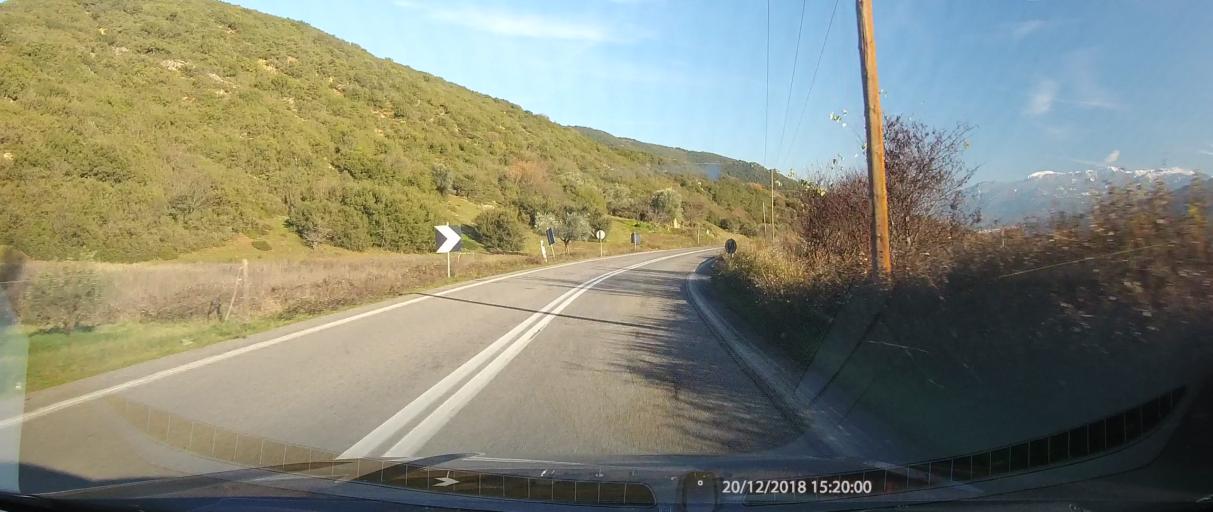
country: GR
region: Central Greece
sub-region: Nomos Fthiotidos
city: Makrakomi
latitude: 38.9370
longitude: 22.0500
